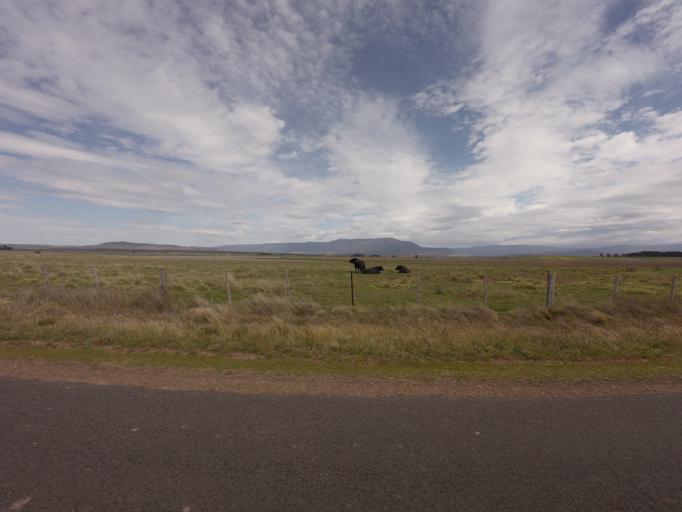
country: AU
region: Tasmania
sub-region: Northern Midlands
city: Evandale
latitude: -41.8075
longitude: 147.2799
